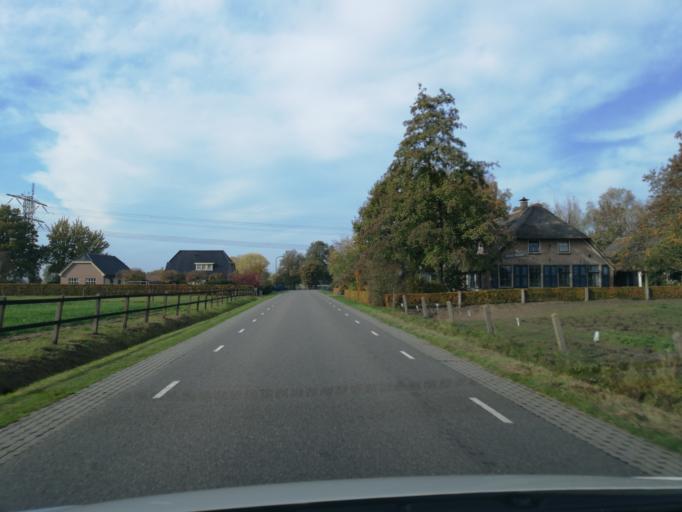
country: NL
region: Gelderland
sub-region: Gemeente Epe
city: Vaassen
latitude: 52.2561
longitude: 6.0142
